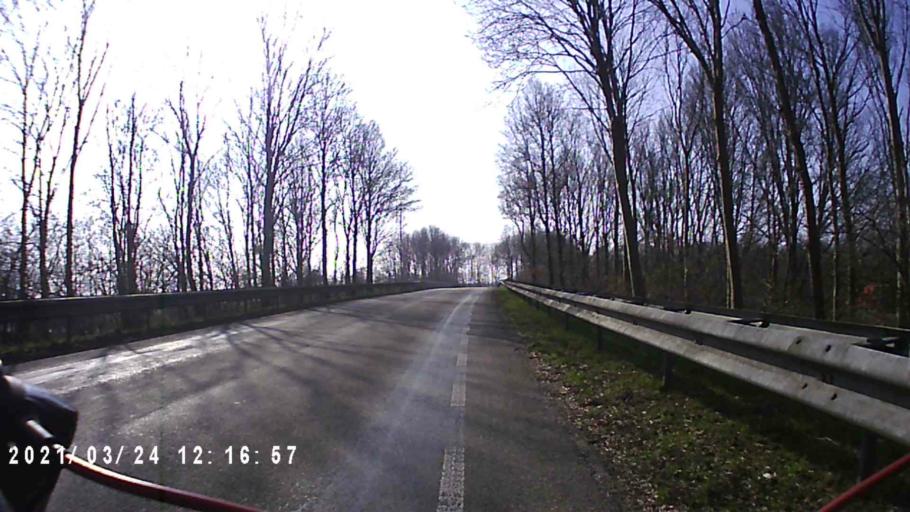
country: NL
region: Groningen
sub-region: Gemeente Zuidhorn
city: Zuidhorn
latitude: 53.1957
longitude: 6.4243
